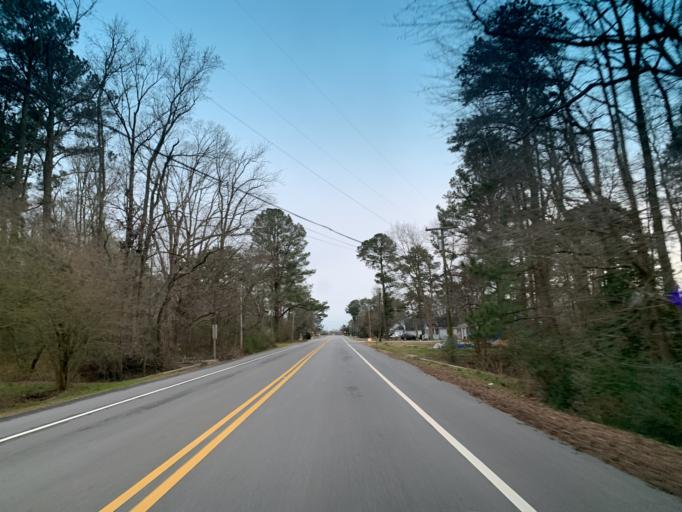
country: US
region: Maryland
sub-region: Worcester County
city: Pocomoke City
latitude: 38.0716
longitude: -75.5465
